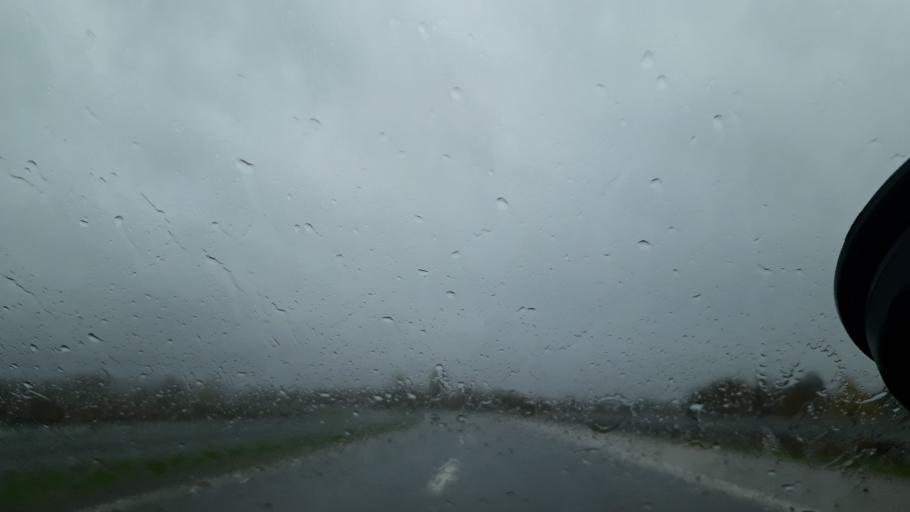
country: BA
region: Republika Srpska
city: Stanari
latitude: 44.8390
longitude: 17.8050
